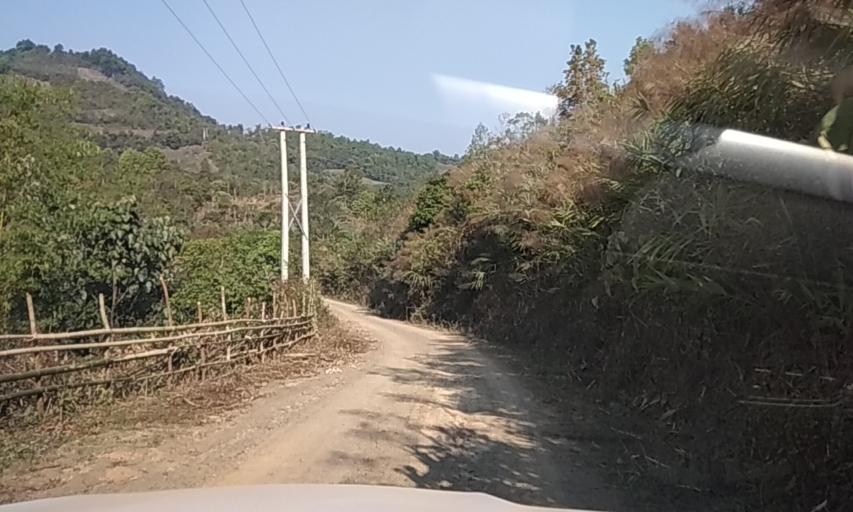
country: LA
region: Phongsali
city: Phongsali
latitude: 21.6937
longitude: 102.0886
